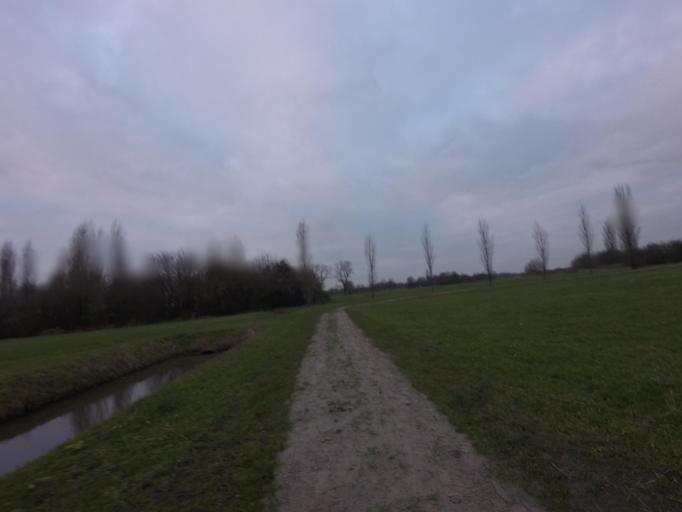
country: NL
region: Utrecht
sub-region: Stichtse Vecht
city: Spechtenkamp
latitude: 52.1175
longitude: 5.0124
